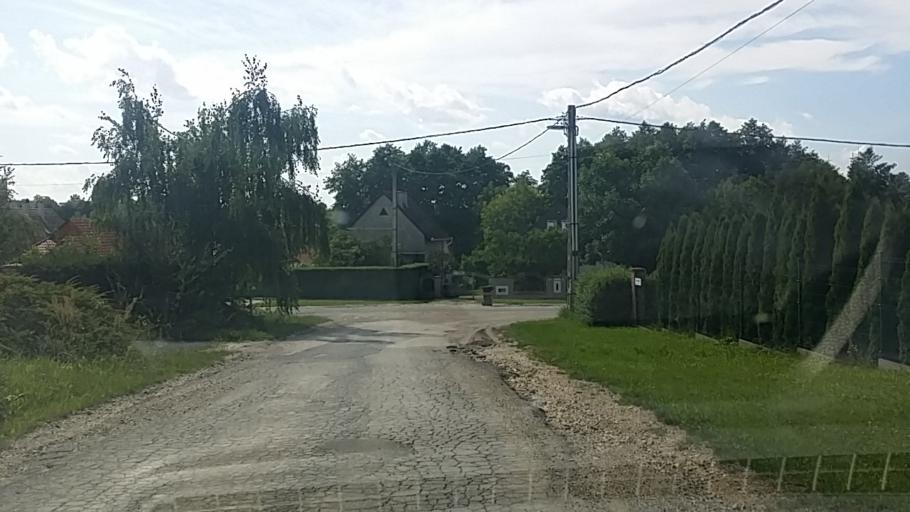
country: HU
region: Zala
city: Nagykanizsa
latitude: 46.4647
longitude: 17.0265
